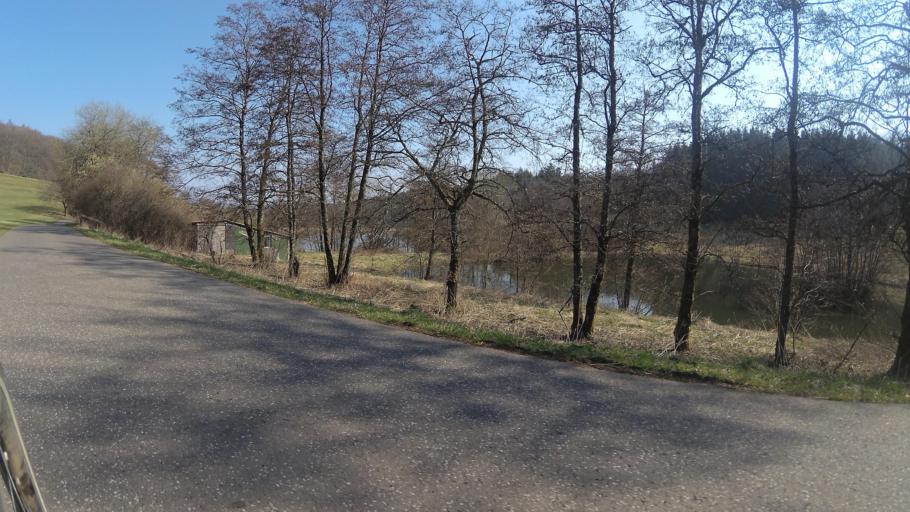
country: DE
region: Rheinland-Pfalz
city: Rohrbach
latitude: 49.5729
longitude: 7.2565
